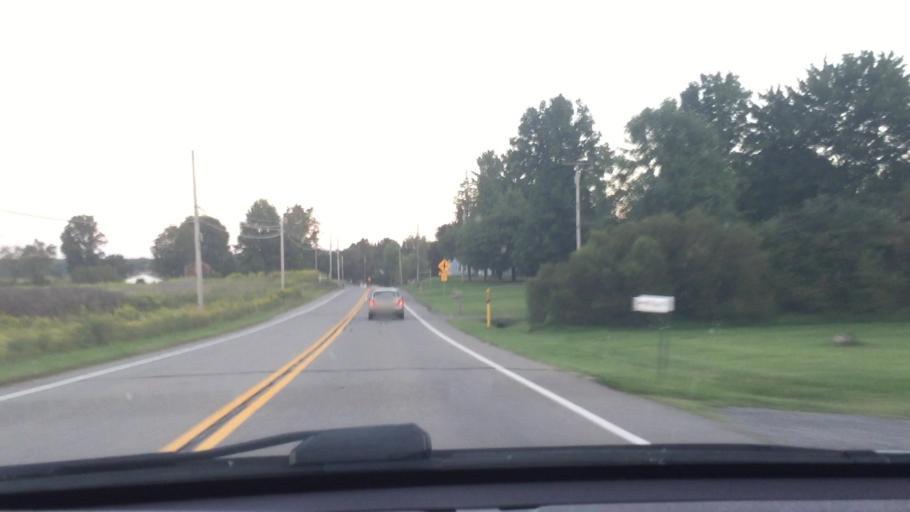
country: US
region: Pennsylvania
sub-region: Mercer County
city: Grove City
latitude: 41.1373
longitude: -80.0772
